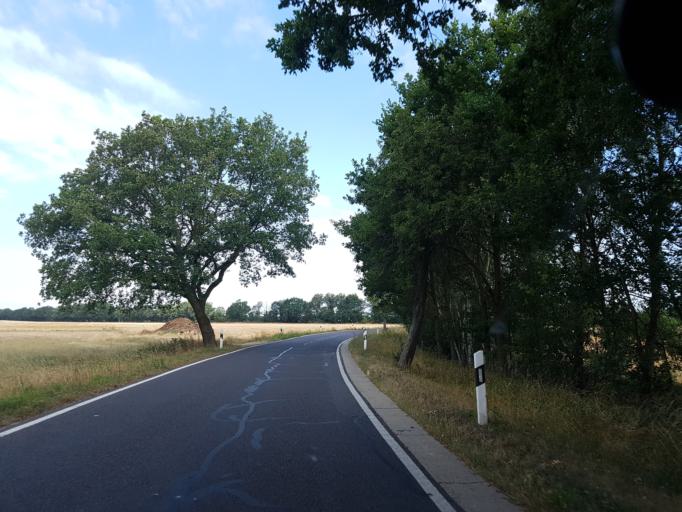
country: DE
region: Brandenburg
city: Luckau
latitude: 51.8430
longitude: 13.6300
